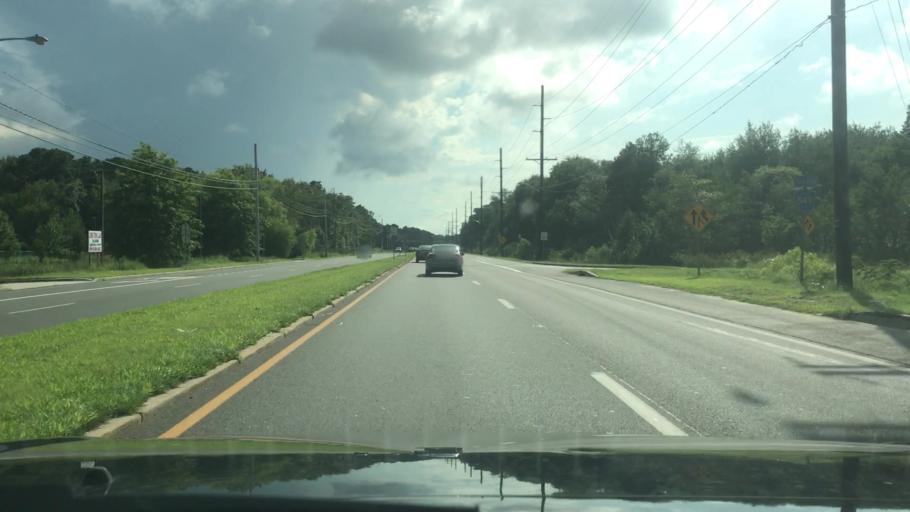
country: US
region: New Jersey
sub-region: Ocean County
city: Leisure Village East
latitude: 40.0030
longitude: -74.1558
